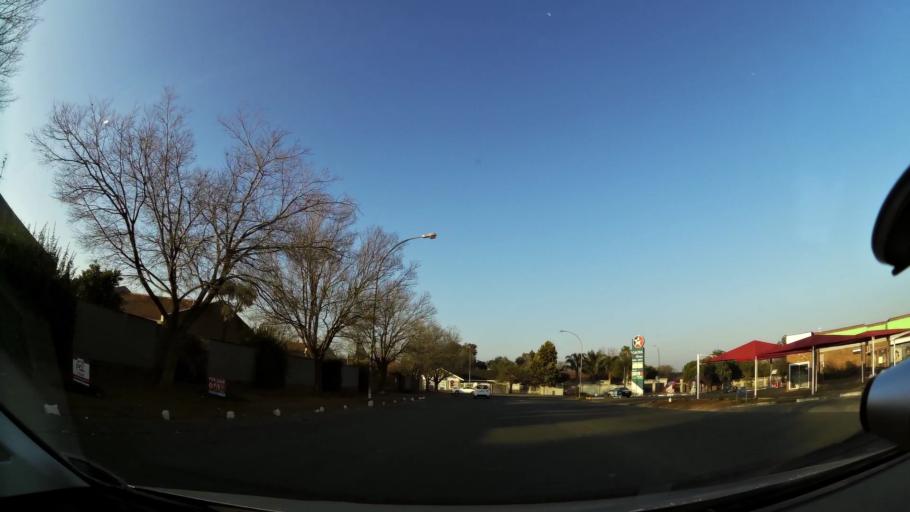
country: ZA
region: Orange Free State
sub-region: Mangaung Metropolitan Municipality
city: Bloemfontein
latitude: -29.1010
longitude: 26.1600
